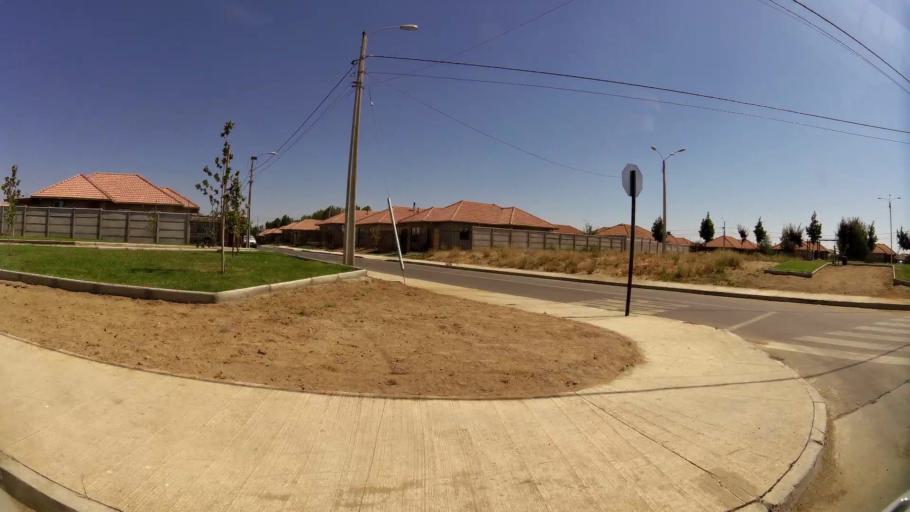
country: CL
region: Maule
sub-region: Provincia de Talca
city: Talca
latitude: -35.4333
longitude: -71.5940
